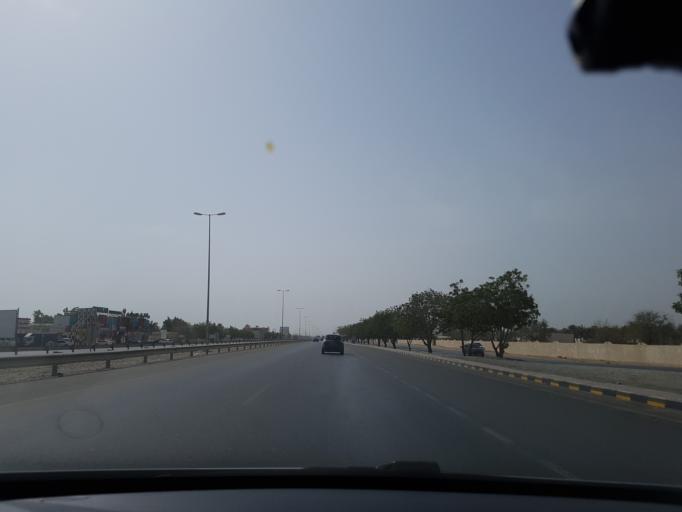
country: OM
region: Al Batinah
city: Al Khaburah
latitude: 23.9691
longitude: 57.0924
